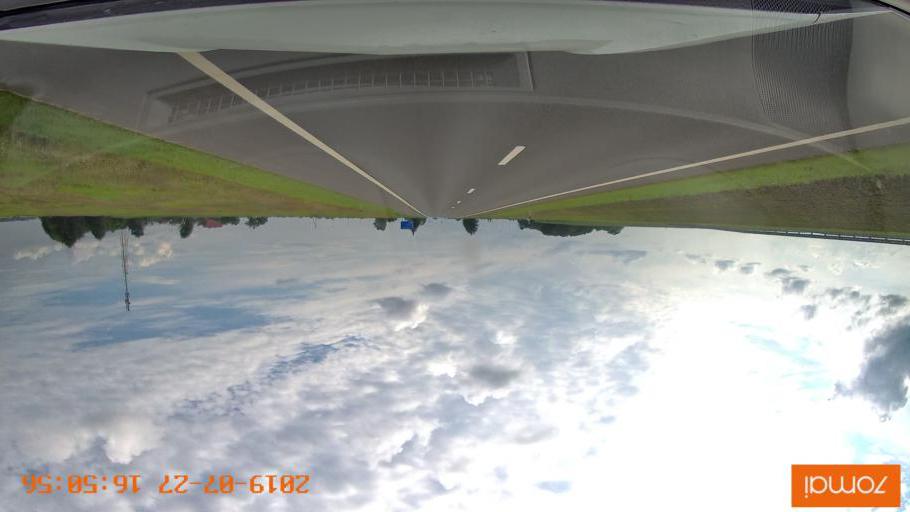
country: RU
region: Kaliningrad
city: Gvardeysk
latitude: 54.6801
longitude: 20.9003
